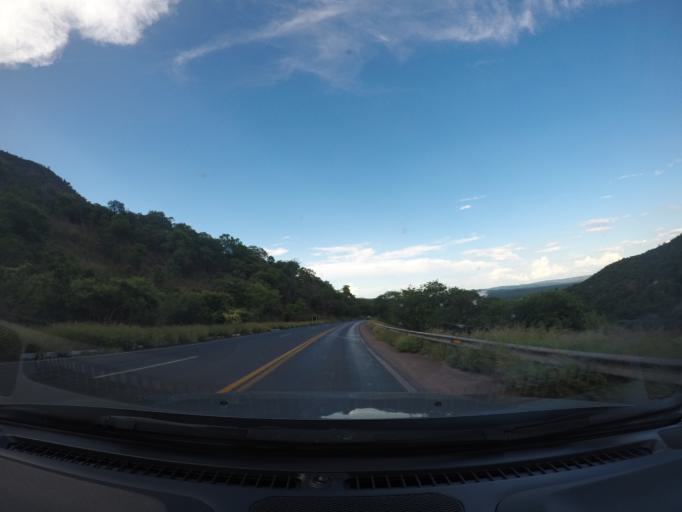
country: BR
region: Bahia
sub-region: Ibotirama
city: Ibotirama
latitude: -12.1358
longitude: -43.3511
